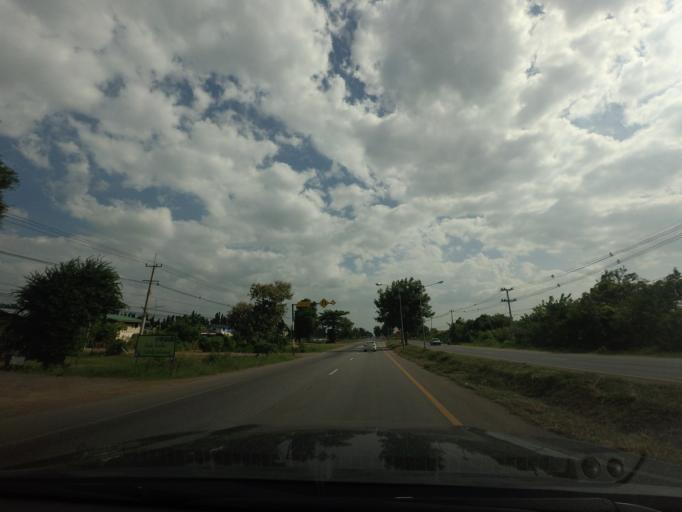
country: TH
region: Lop Buri
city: Chai Badan
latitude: 15.2566
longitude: 101.1252
